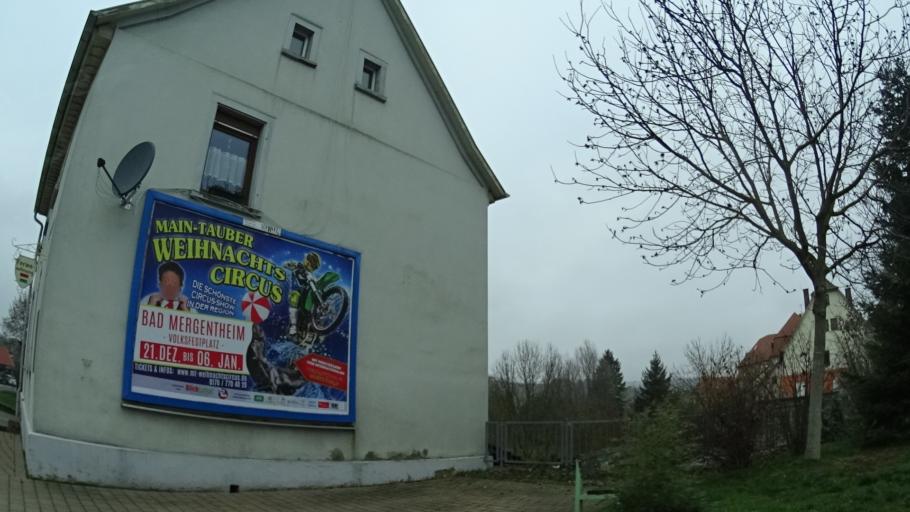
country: DE
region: Baden-Wuerttemberg
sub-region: Regierungsbezirk Stuttgart
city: Boxberg
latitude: 49.4789
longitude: 9.6392
